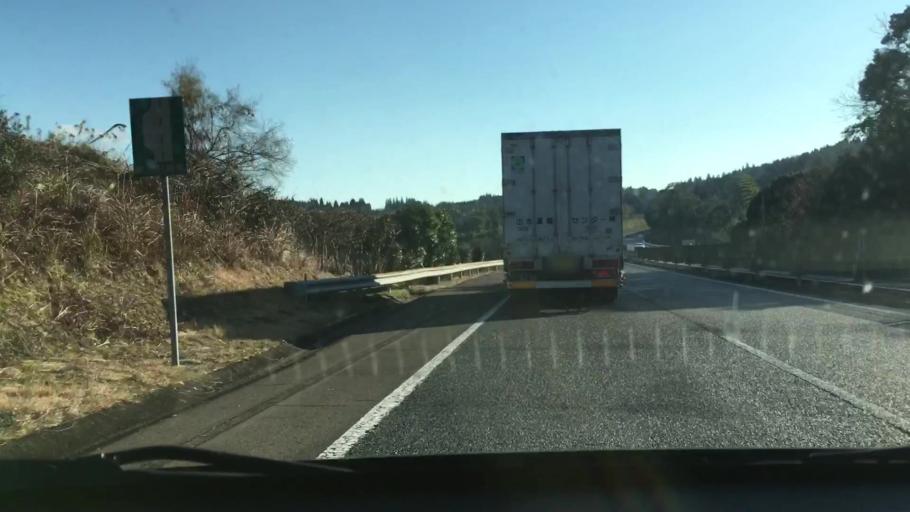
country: JP
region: Kagoshima
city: Kajiki
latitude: 31.8797
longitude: 130.6953
